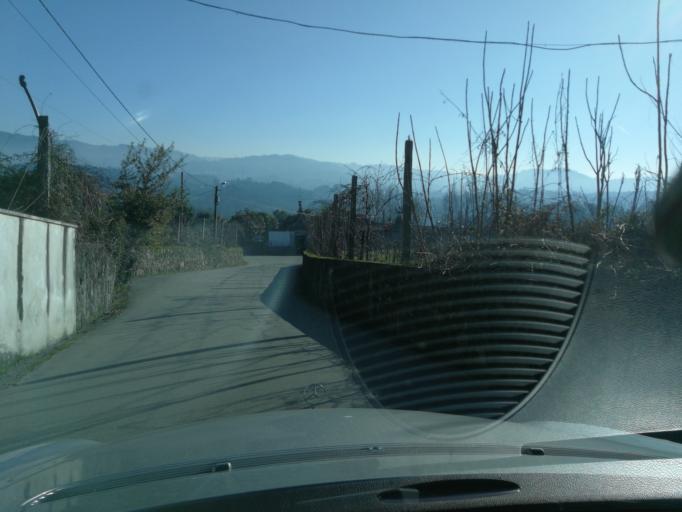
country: PT
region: Braga
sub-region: Braga
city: Adaufe
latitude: 41.6133
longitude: -8.3977
